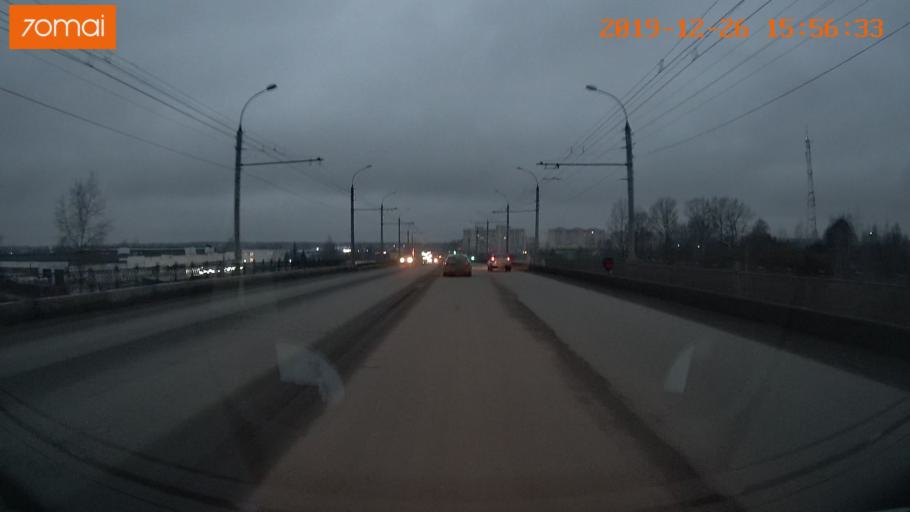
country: RU
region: Jaroslavl
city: Rybinsk
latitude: 58.0427
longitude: 38.8000
